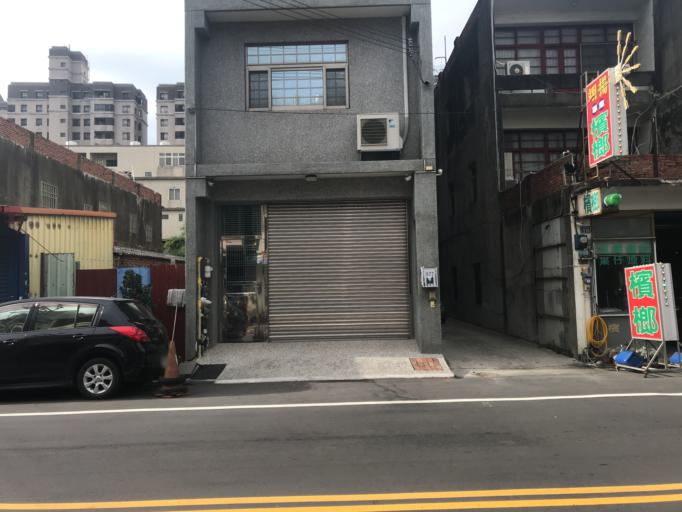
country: TW
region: Taiwan
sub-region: Hsinchu
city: Zhubei
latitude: 24.8204
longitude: 121.0311
